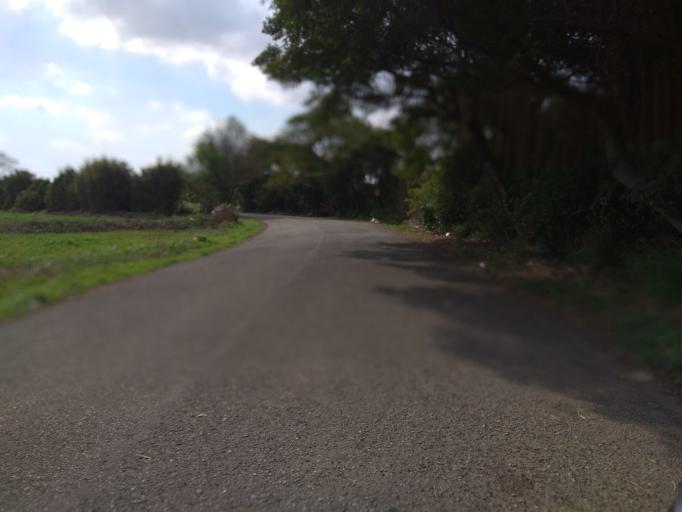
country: TW
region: Taiwan
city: Taoyuan City
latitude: 25.0479
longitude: 121.2284
